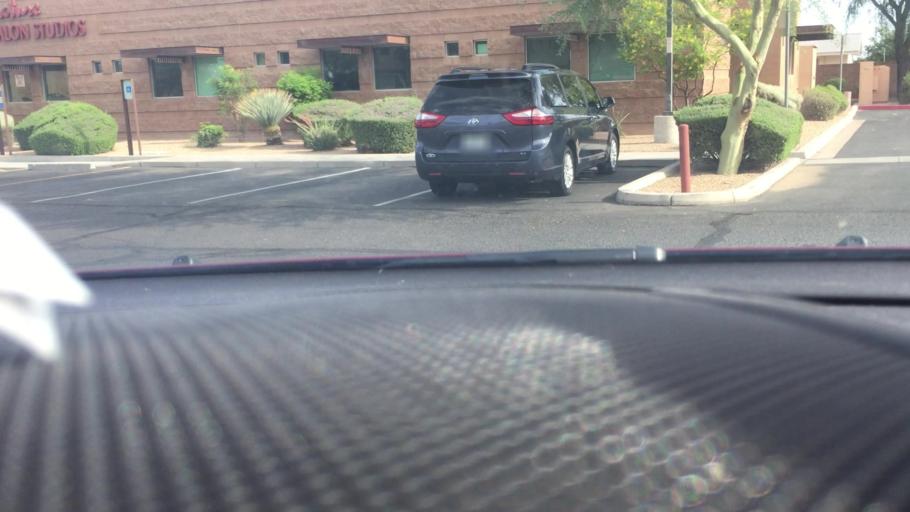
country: US
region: Arizona
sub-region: Maricopa County
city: Gilbert
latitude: 33.3948
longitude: -111.7209
